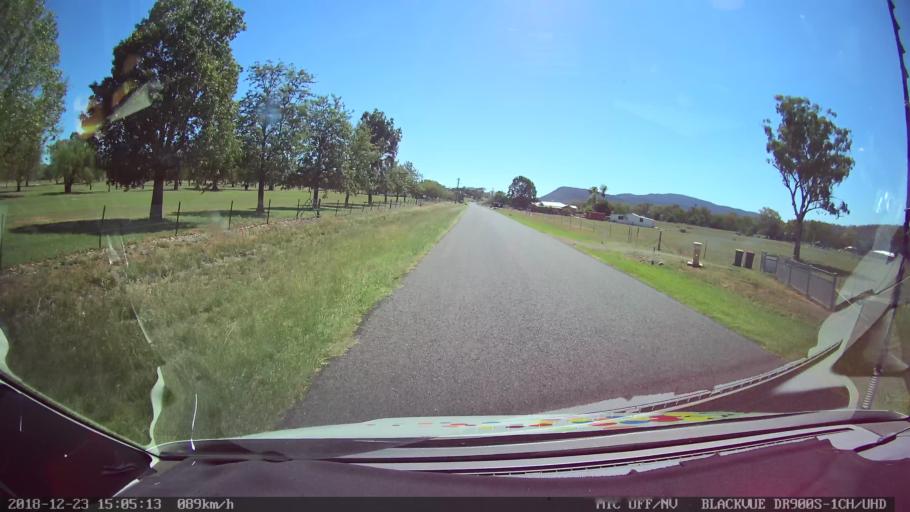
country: AU
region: New South Wales
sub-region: Tamworth Municipality
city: Manilla
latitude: -30.7436
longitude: 150.7407
